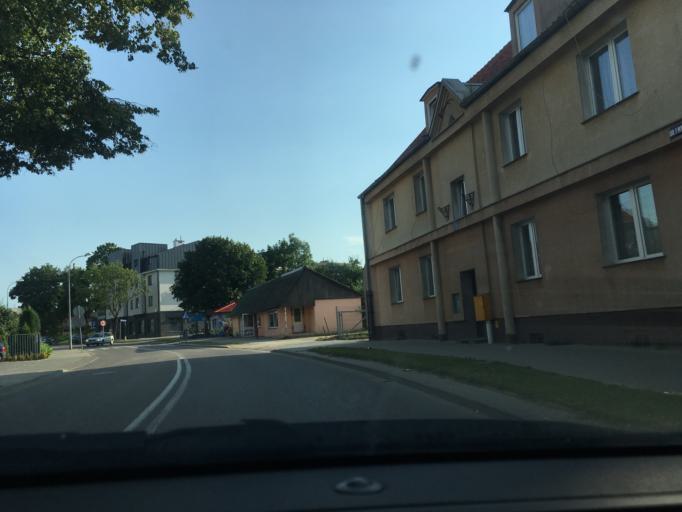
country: PL
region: Warmian-Masurian Voivodeship
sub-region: Powiat olecki
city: Olecko
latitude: 54.0329
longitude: 22.5071
